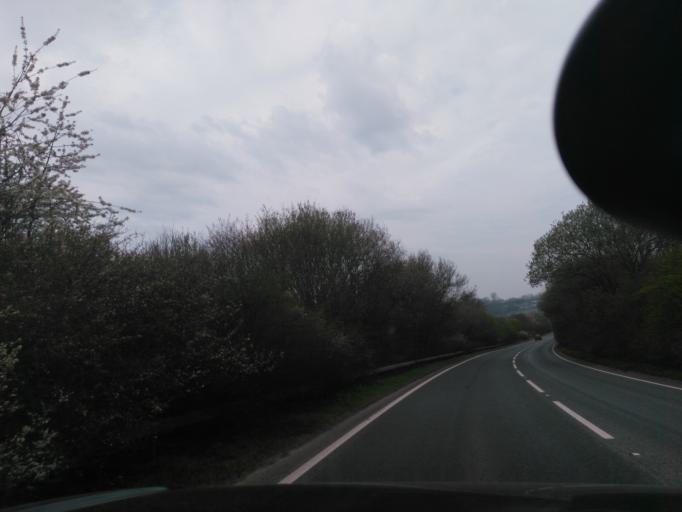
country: GB
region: England
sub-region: Somerset
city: Frome
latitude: 51.2072
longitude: -2.3222
